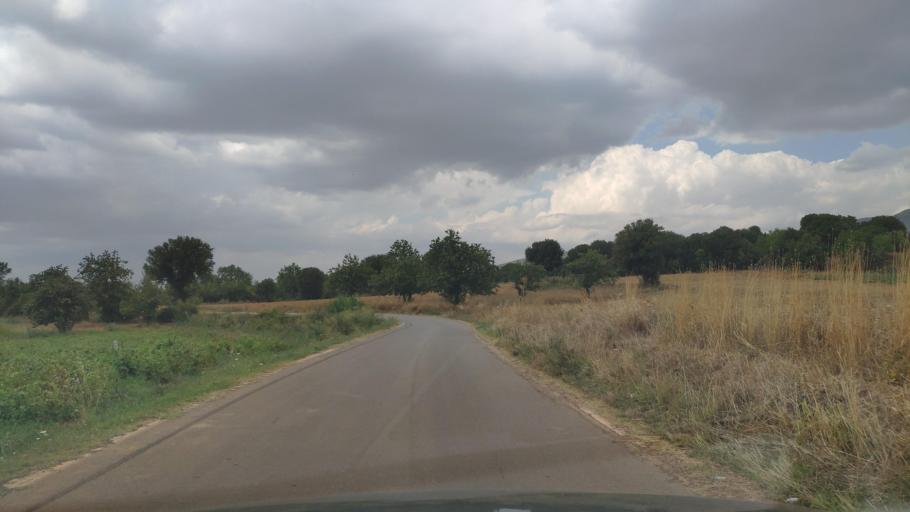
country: GR
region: Peloponnese
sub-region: Nomos Lakonias
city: Kariai
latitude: 37.3197
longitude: 22.4374
